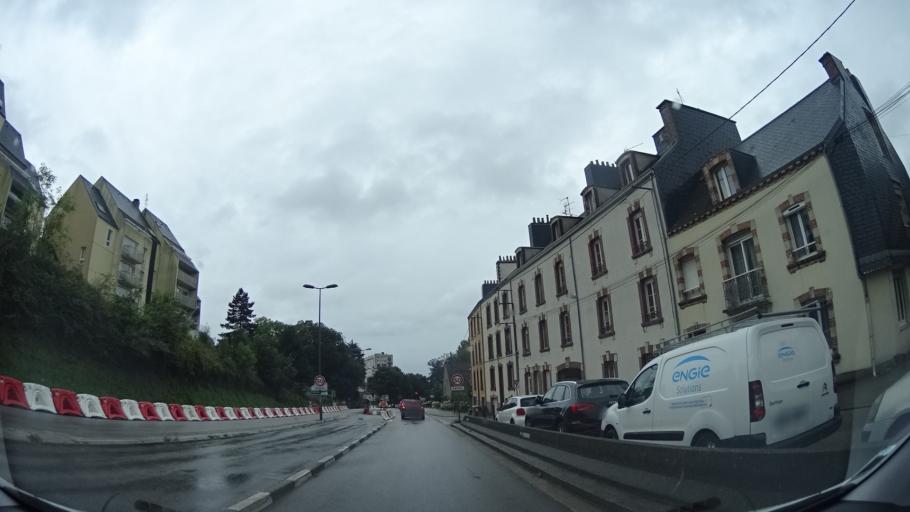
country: FR
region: Lower Normandy
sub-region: Departement de la Manche
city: Cherbourg-Octeville
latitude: 49.6313
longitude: -1.6239
